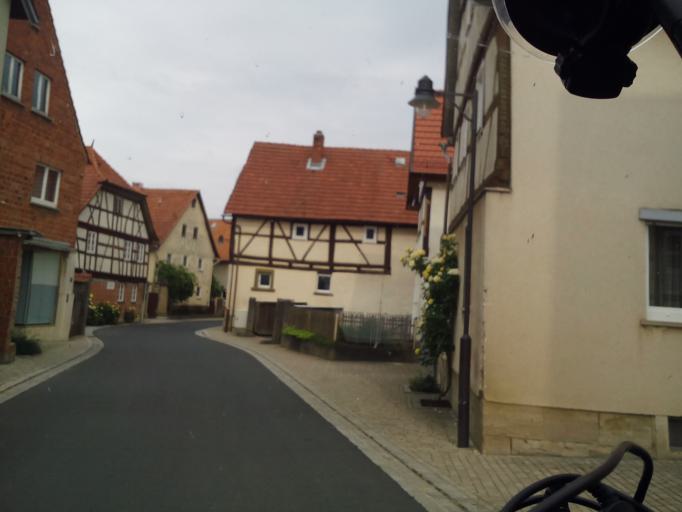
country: DE
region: Bavaria
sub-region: Regierungsbezirk Unterfranken
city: Hendungen
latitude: 50.3950
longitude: 10.3506
